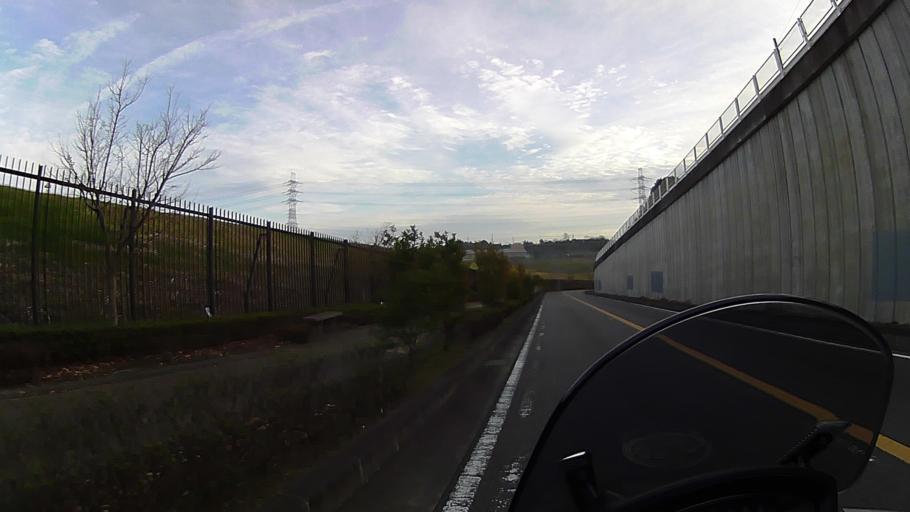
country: JP
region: Kanagawa
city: Atsugi
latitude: 35.4219
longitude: 139.4180
